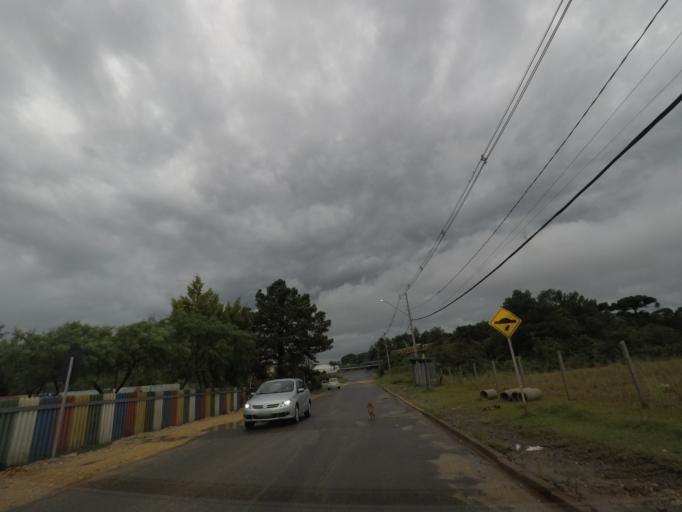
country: BR
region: Parana
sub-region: Campo Largo
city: Campo Largo
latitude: -25.4448
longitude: -49.4605
